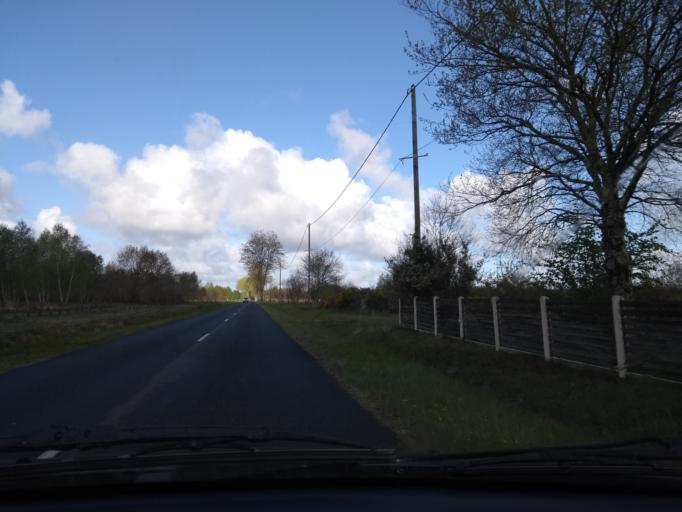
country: FR
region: Aquitaine
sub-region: Departement de la Gironde
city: Mios
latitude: 44.5498
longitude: -0.9816
